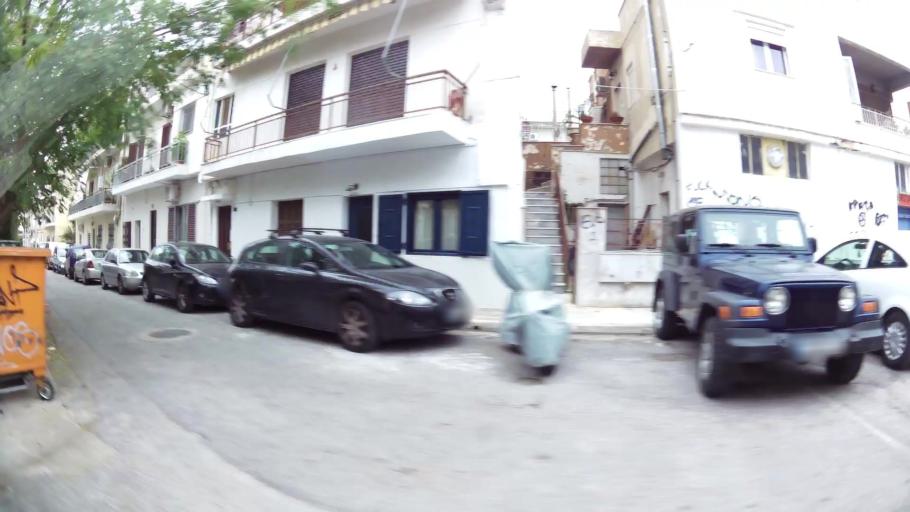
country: GR
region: Attica
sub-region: Nomarchia Athinas
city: Chaidari
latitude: 37.9976
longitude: 23.6747
